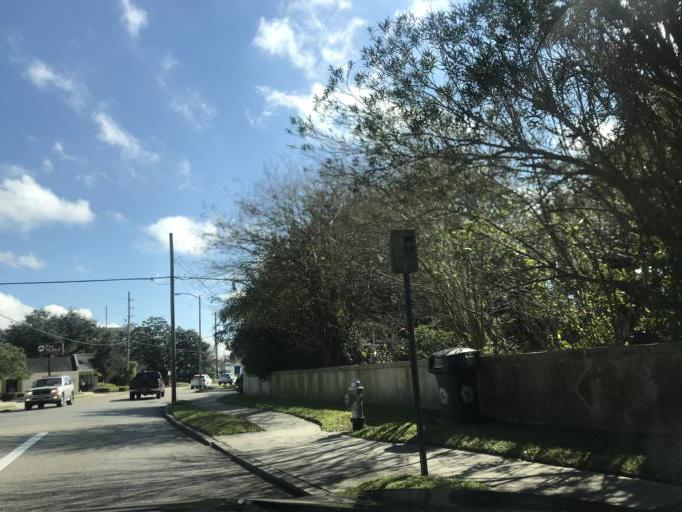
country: US
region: Louisiana
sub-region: Jefferson Parish
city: Metairie
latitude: 29.9890
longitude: -90.1327
